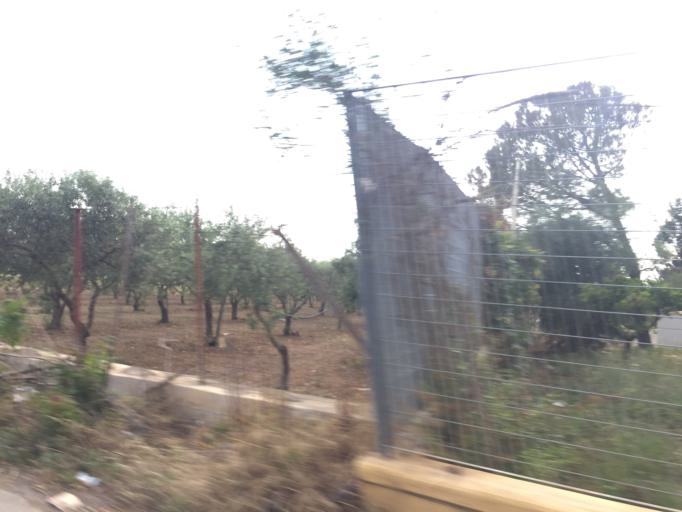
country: IT
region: Apulia
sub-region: Provincia di Bari
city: Capurso
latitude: 41.0548
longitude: 16.9215
